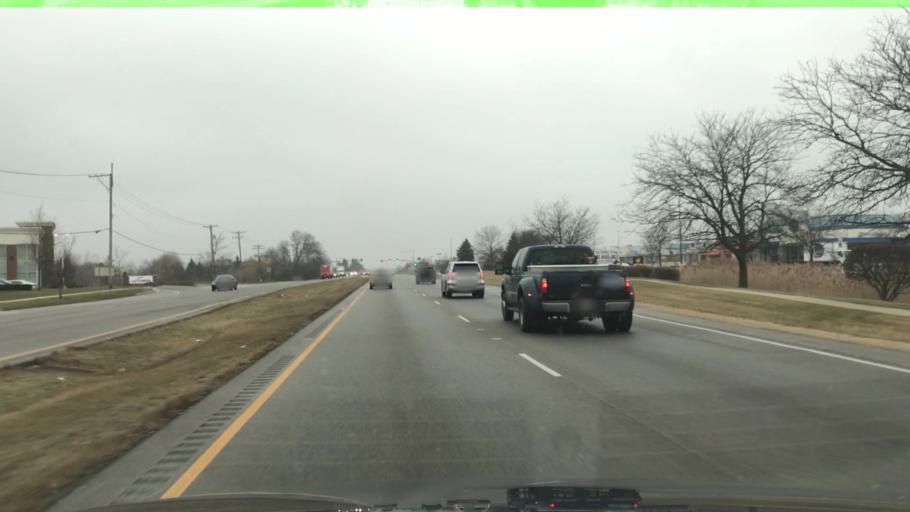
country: US
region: Illinois
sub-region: Lake County
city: Lake Zurich
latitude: 42.1839
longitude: -88.0884
